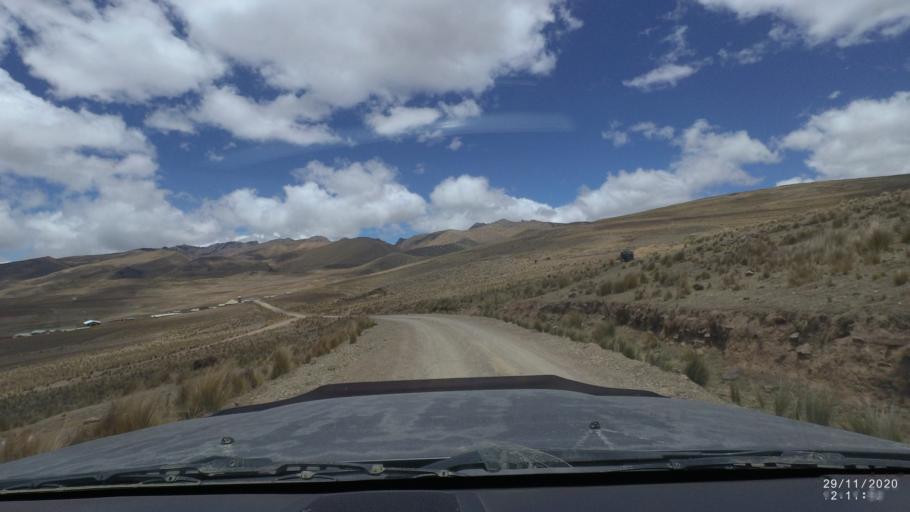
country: BO
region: Cochabamba
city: Cochabamba
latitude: -17.1163
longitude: -66.3038
